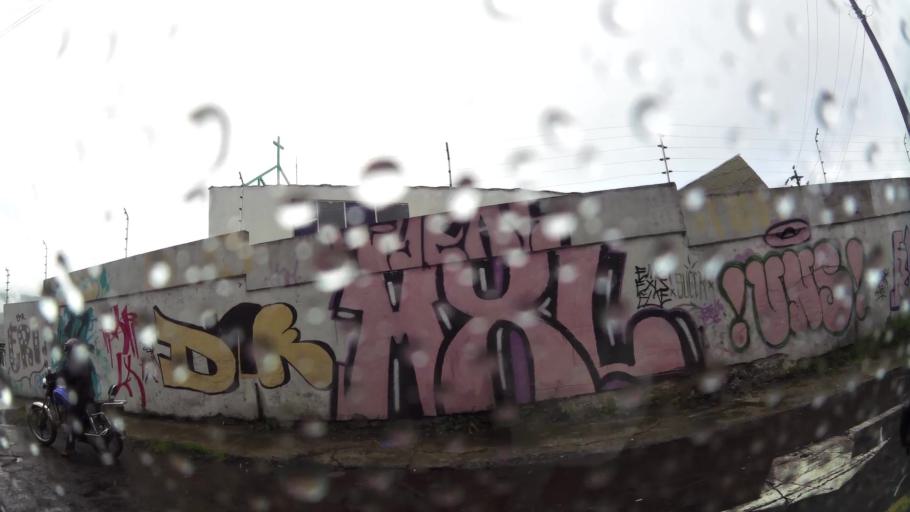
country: EC
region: Pichincha
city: Quito
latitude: -0.0873
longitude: -78.5107
